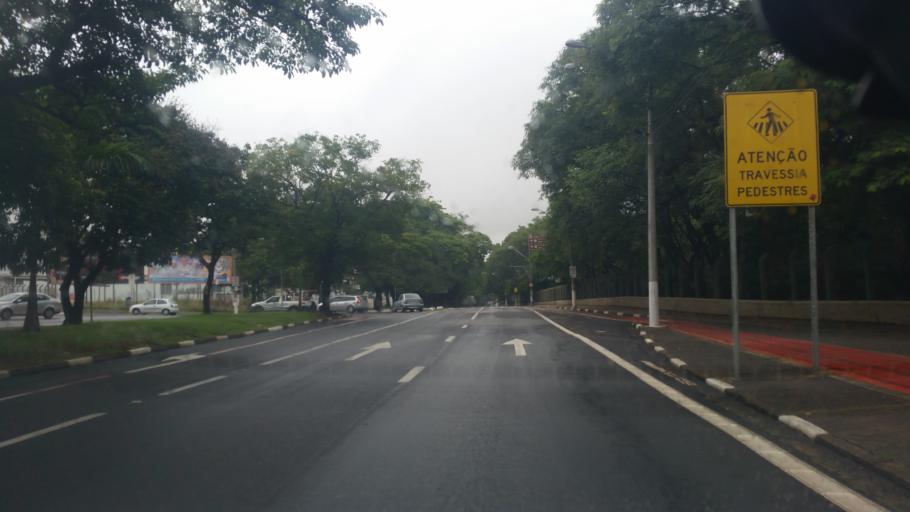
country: BR
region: Sao Paulo
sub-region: Campinas
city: Campinas
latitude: -22.8752
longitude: -47.0469
